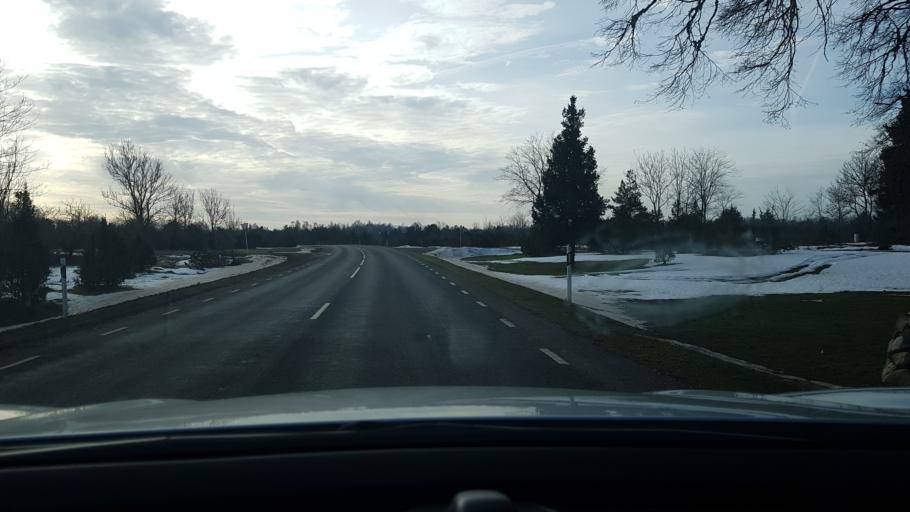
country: EE
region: Saare
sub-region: Kuressaare linn
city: Kuressaare
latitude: 58.2907
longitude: 22.5402
